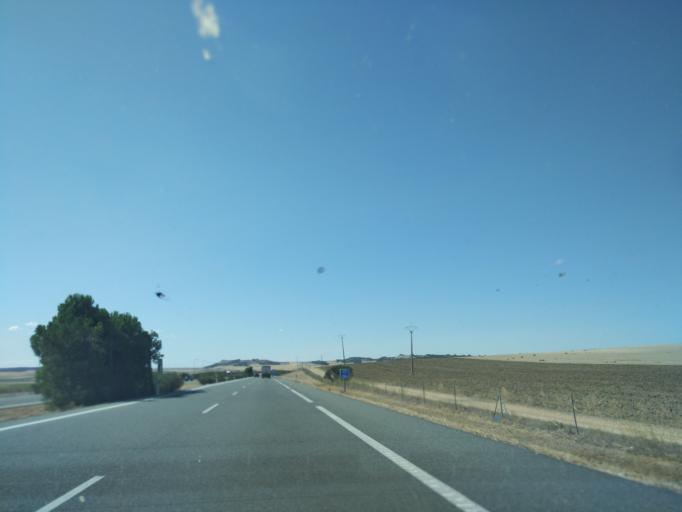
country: ES
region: Castille and Leon
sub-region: Provincia de Valladolid
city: Vega de Valdetronco
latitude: 41.5766
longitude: -5.0992
